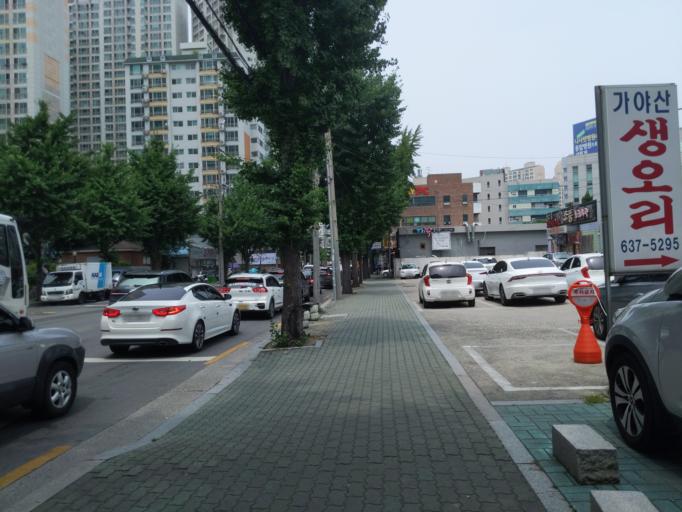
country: KR
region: Daegu
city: Hwawon
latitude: 35.8122
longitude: 128.5252
